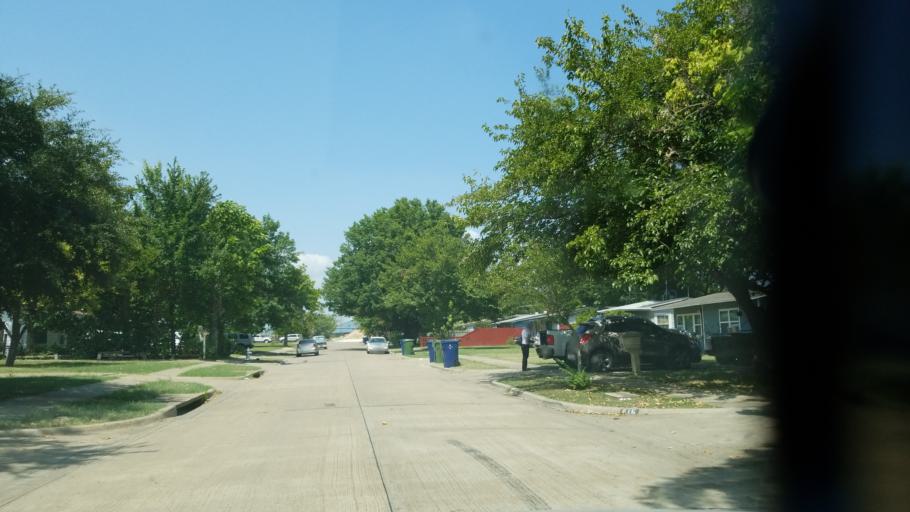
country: US
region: Texas
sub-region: Dallas County
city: Garland
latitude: 32.9196
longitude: -96.6347
